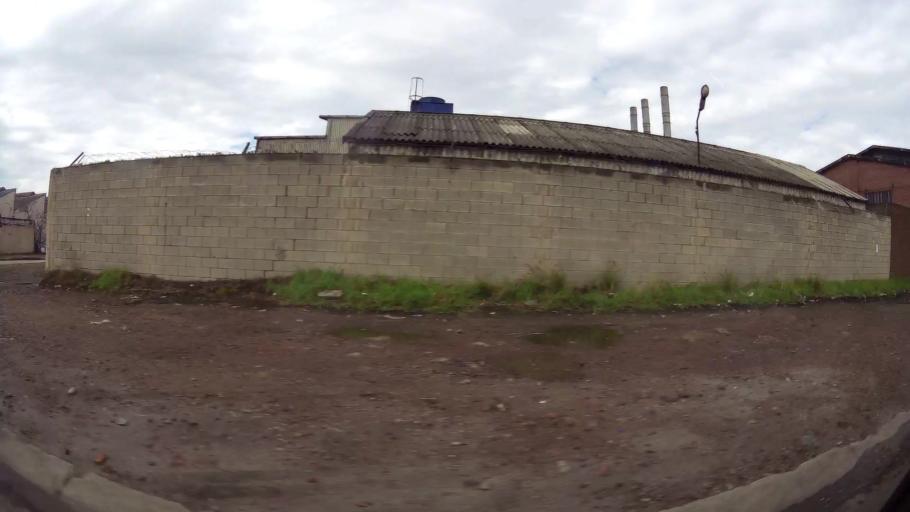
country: ZA
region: Eastern Cape
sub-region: Nelson Mandela Bay Metropolitan Municipality
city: Port Elizabeth
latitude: -33.9292
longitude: 25.5787
